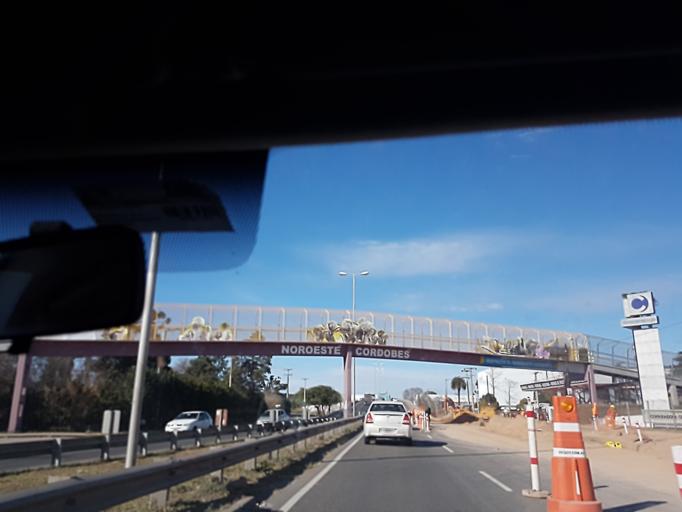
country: AR
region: Cordoba
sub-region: Departamento de Capital
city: Cordoba
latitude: -31.3404
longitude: -64.2079
